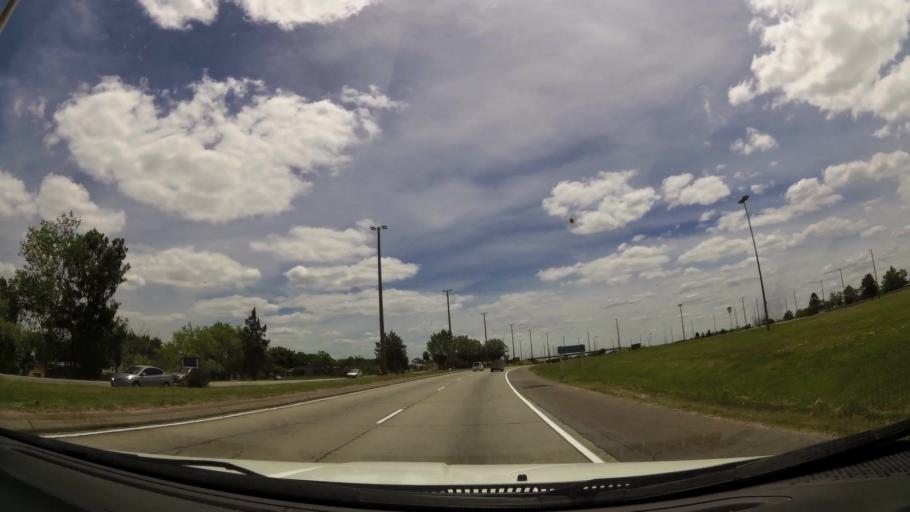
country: UY
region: Montevideo
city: Montevideo
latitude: -34.8615
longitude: -56.2558
